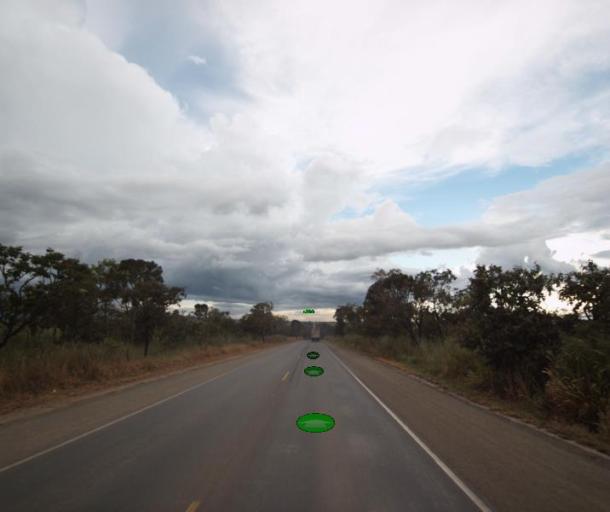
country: BR
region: Goias
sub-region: Itapaci
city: Itapaci
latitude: -14.8256
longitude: -49.3008
